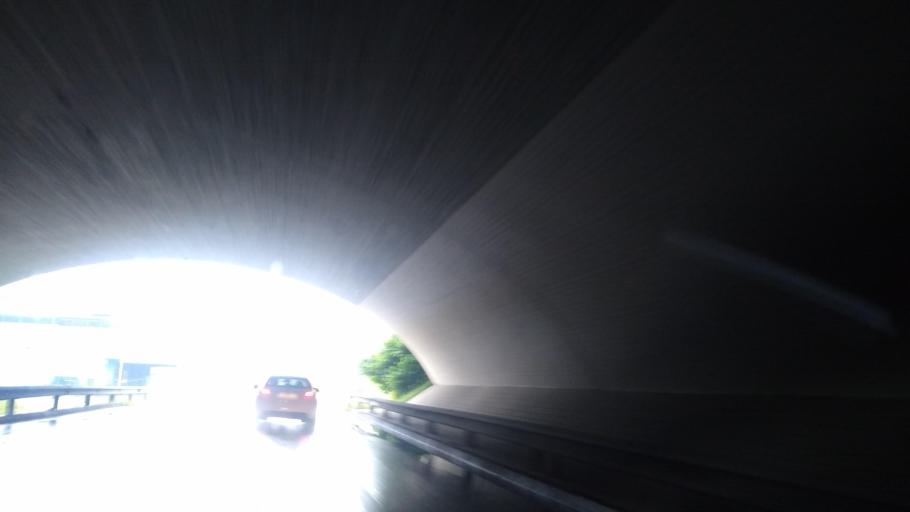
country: AT
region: Tyrol
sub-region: Politischer Bezirk Innsbruck Land
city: Volders
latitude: 47.2825
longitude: 11.5420
